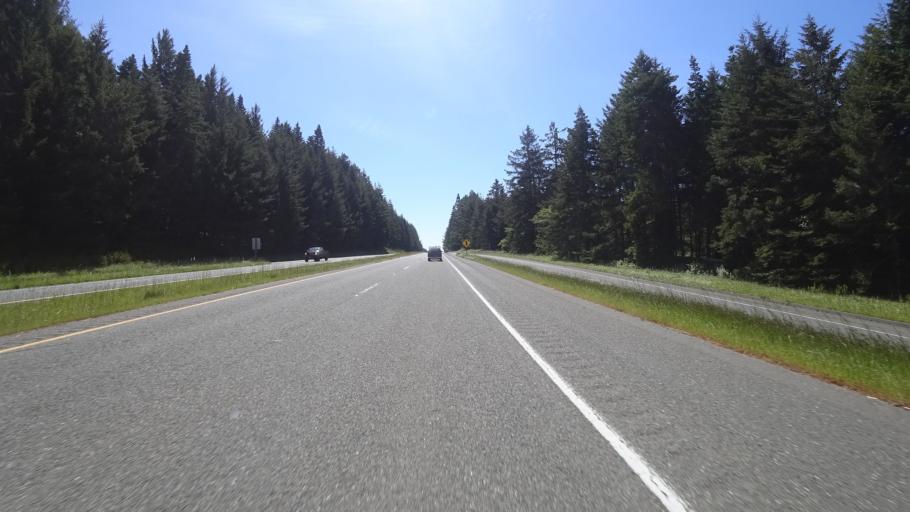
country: US
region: California
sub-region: Humboldt County
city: Westhaven-Moonstone
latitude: 41.0975
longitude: -124.1530
